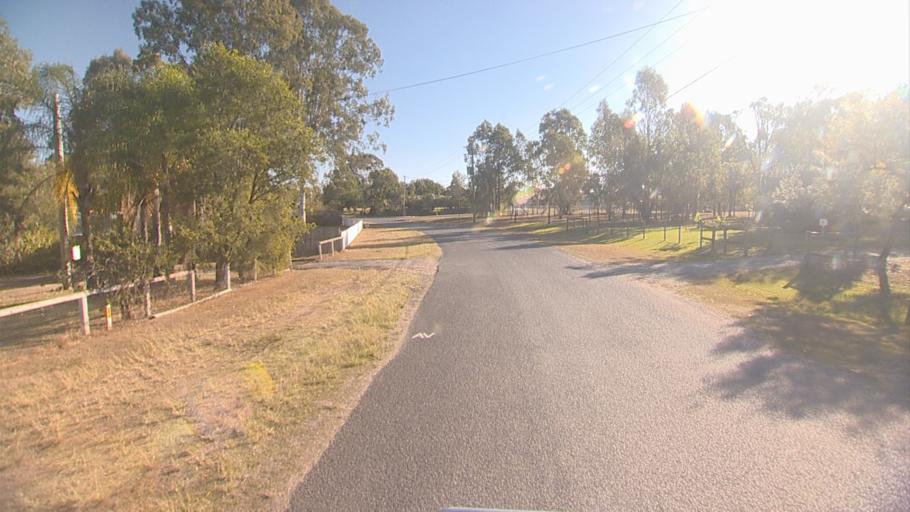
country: AU
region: Queensland
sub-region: Logan
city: Cedar Vale
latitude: -27.8286
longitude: 153.0215
